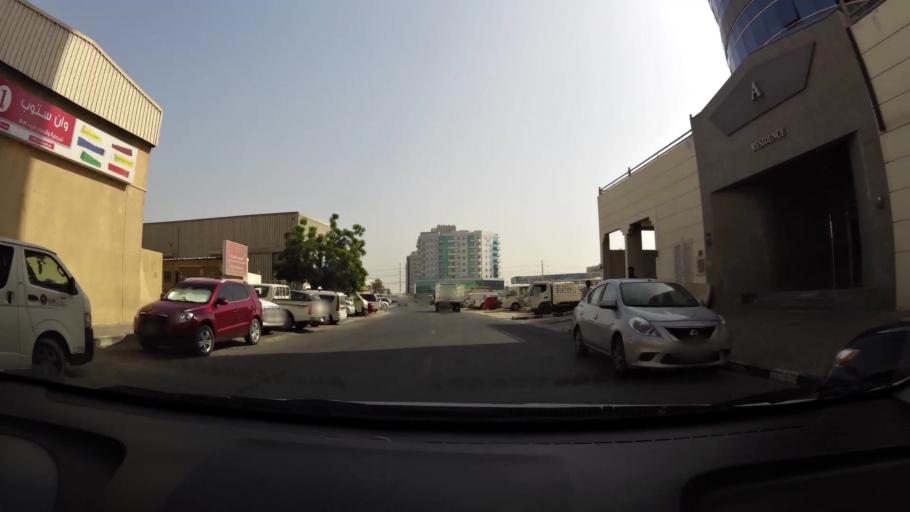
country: AE
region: Ash Shariqah
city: Sharjah
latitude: 25.2938
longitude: 55.3948
